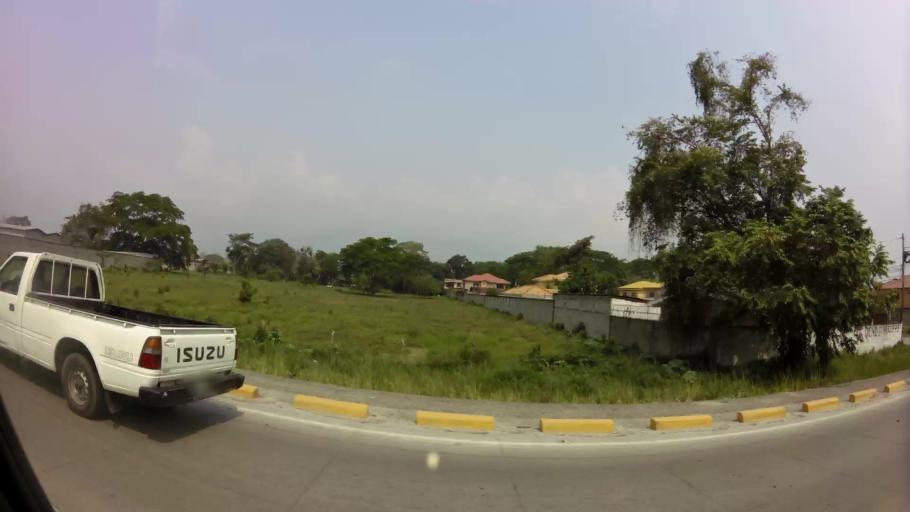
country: HN
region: Cortes
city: San Pedro Sula
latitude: 15.5409
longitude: -87.9992
